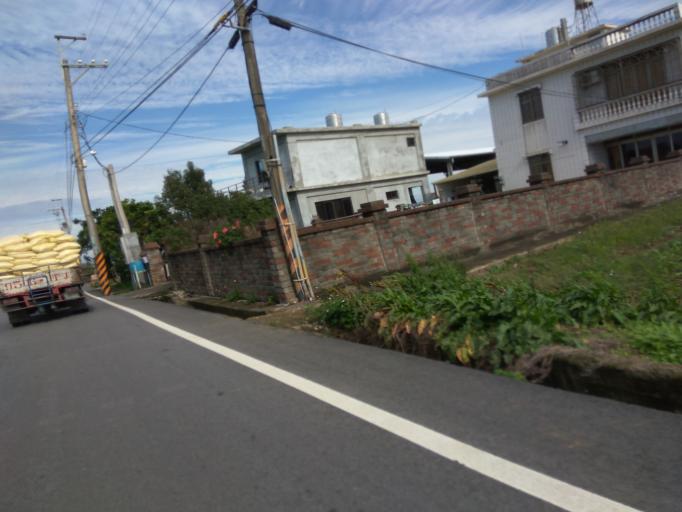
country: TW
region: Taiwan
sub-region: Hsinchu
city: Zhubei
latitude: 24.9990
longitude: 121.0884
